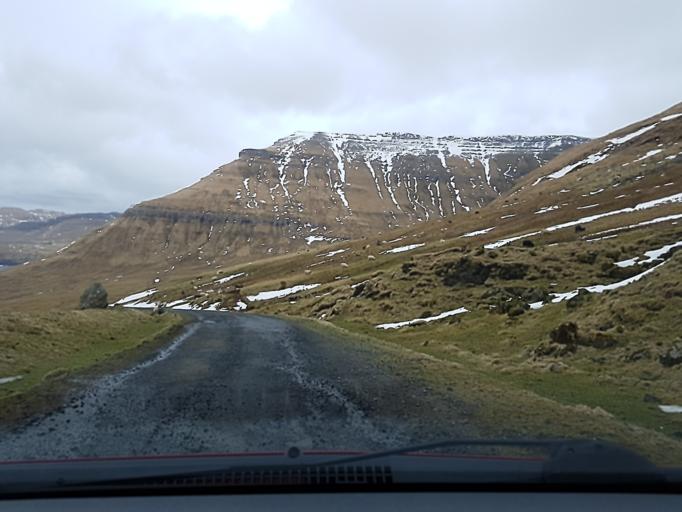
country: FO
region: Streymoy
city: Kollafjordhur
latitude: 62.0191
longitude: -6.9073
